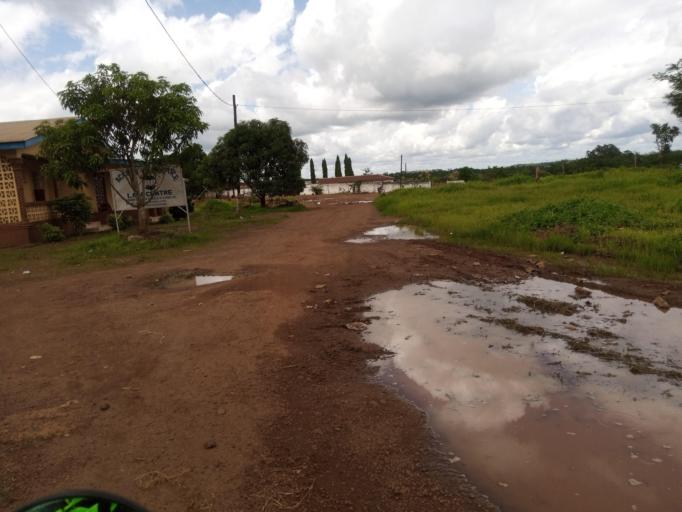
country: SL
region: Northern Province
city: Port Loko
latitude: 8.7689
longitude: -12.7749
